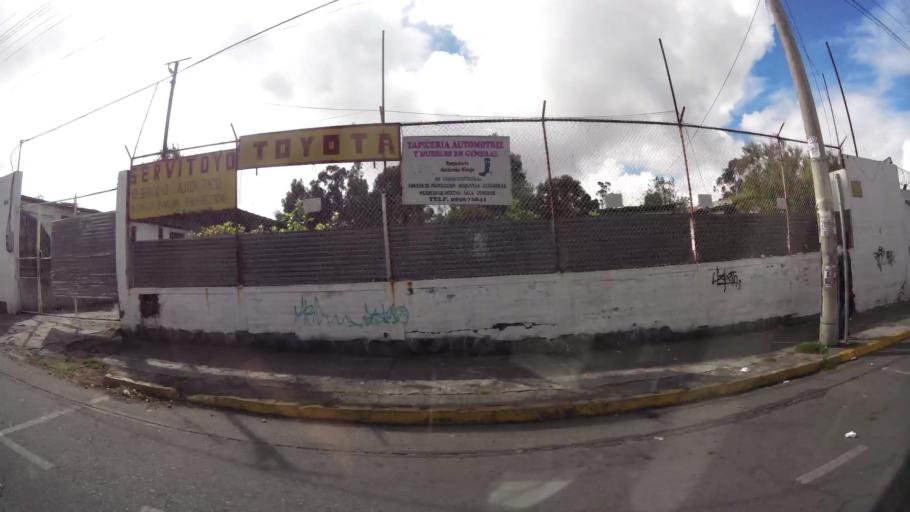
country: EC
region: Pichincha
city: Quito
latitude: -0.1612
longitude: -78.4737
